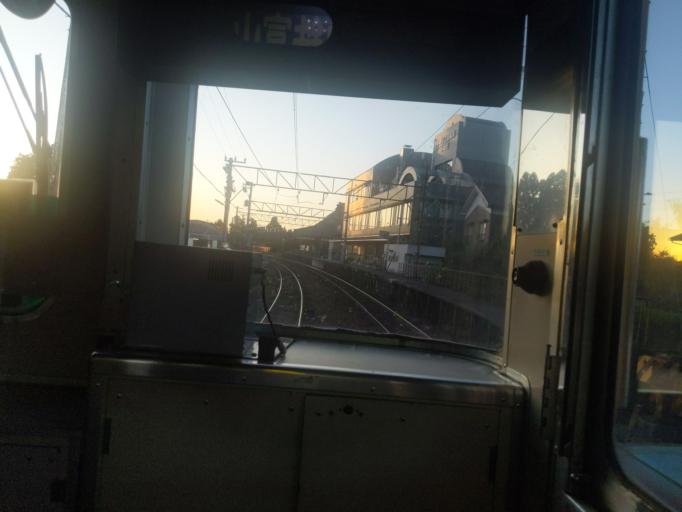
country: JP
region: Toyama
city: Kamiichi
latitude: 36.7054
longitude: 137.3071
